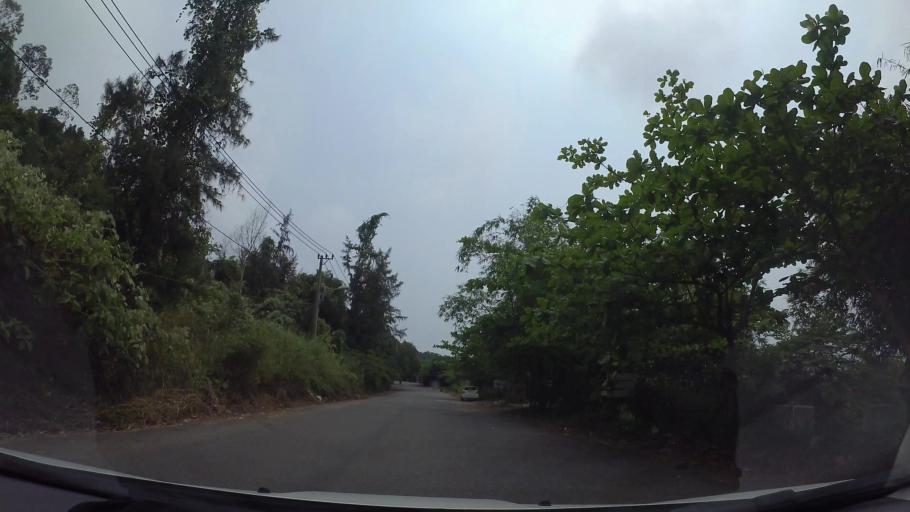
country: VN
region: Da Nang
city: Son Tra
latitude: 16.1049
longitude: 108.3005
